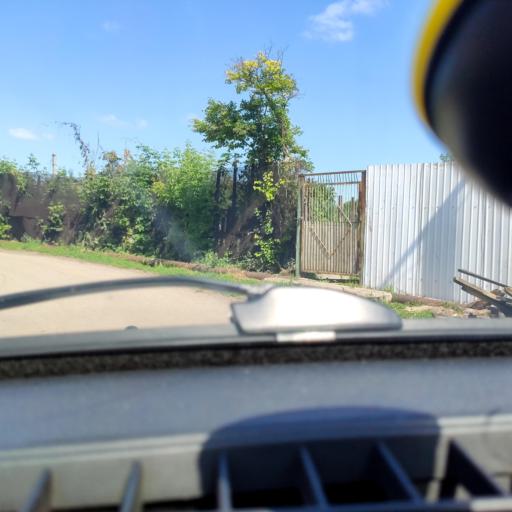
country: RU
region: Samara
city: Tol'yatti
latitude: 53.5581
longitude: 49.4481
